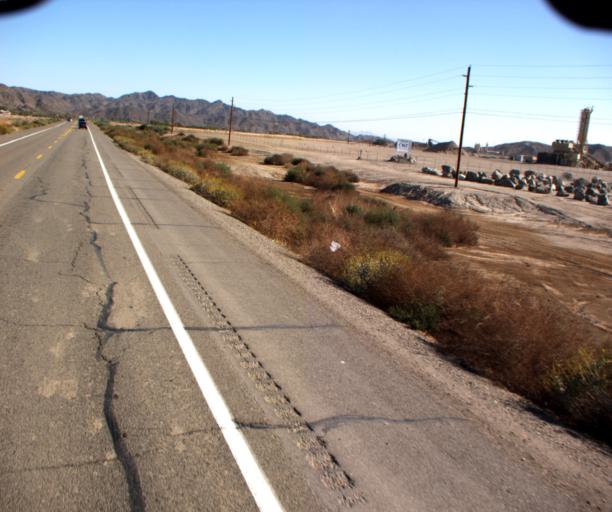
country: US
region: Arizona
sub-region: Yuma County
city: Fortuna Foothills
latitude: 32.7484
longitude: -114.4228
